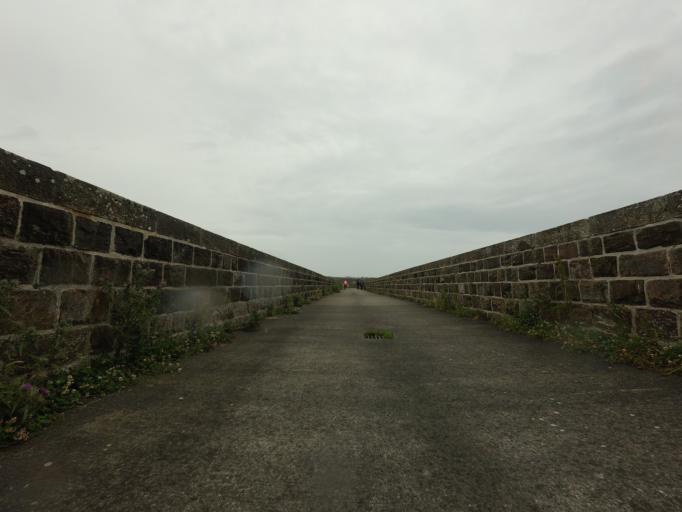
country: GB
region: Scotland
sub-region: Moray
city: Cullen
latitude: 57.6920
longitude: -2.8298
